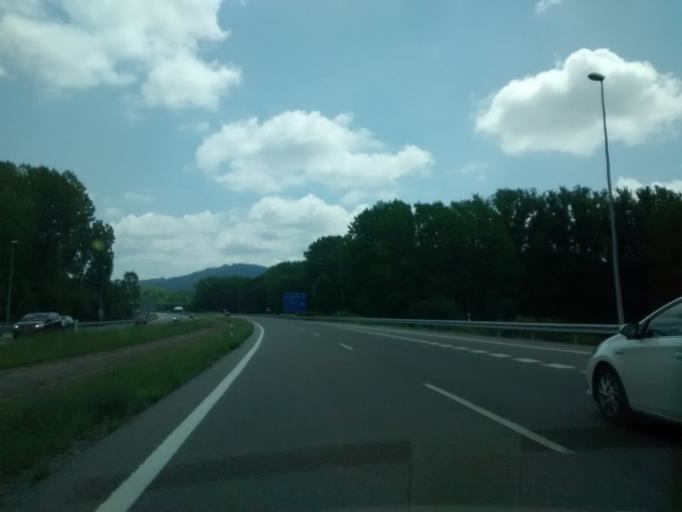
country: ES
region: Castille and Leon
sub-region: Provincia de Leon
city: Camponaraya
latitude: 42.5834
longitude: -6.6249
